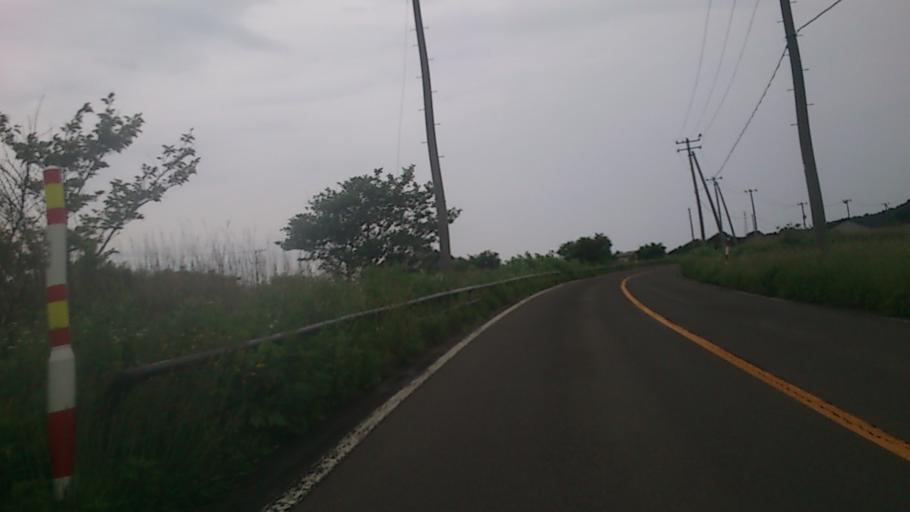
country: JP
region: Akita
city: Noshiromachi
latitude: 40.3777
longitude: 140.0061
